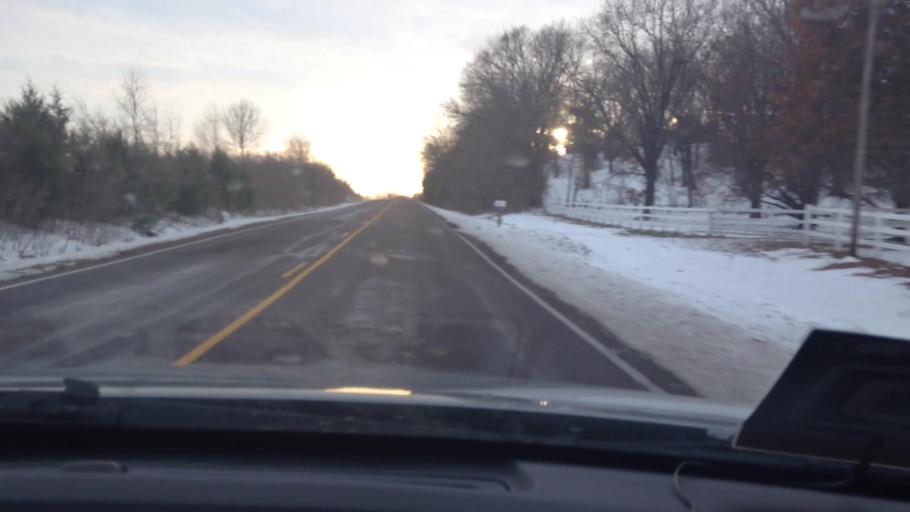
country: US
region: Kansas
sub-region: Leavenworth County
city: Leavenworth
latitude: 39.2705
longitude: -94.9640
